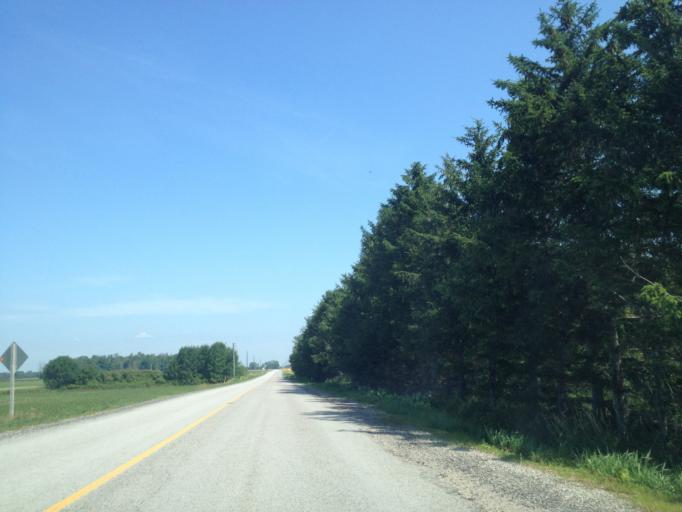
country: CA
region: Ontario
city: London
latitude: 43.1065
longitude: -81.2276
